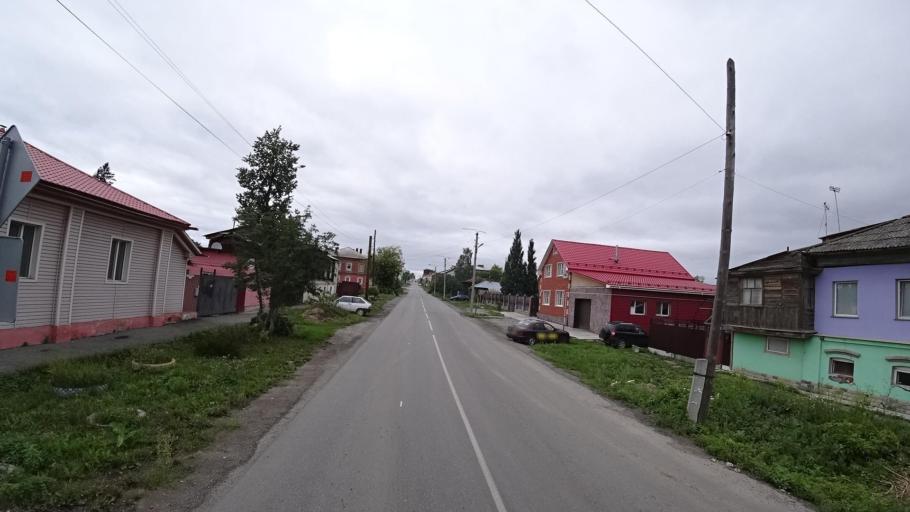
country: RU
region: Sverdlovsk
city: Kamyshlov
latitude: 56.8429
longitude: 62.6978
